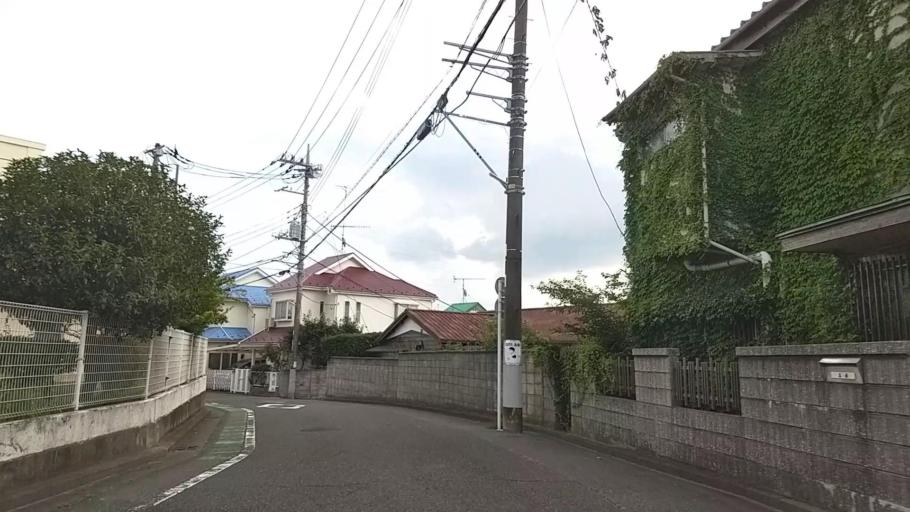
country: JP
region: Kanagawa
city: Yokohama
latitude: 35.4838
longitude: 139.5658
